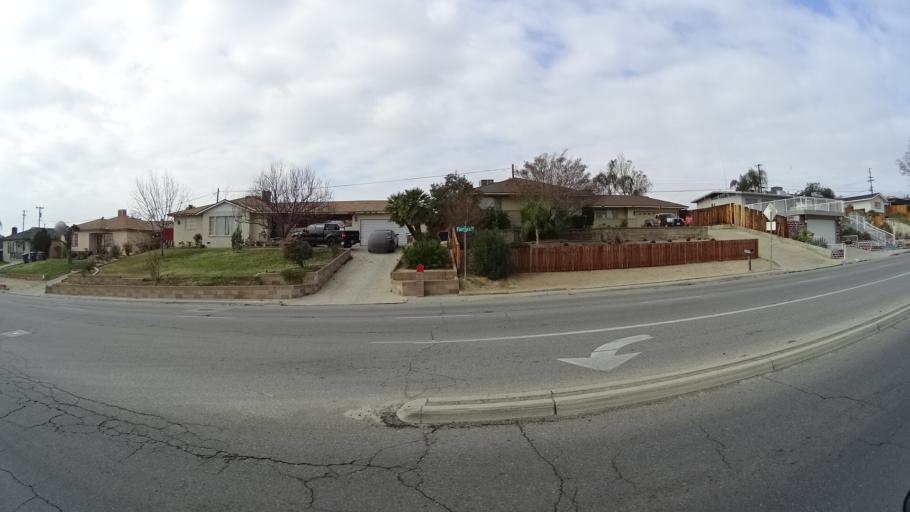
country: US
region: California
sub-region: Kern County
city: Bakersfield
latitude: 35.3770
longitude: -118.9319
